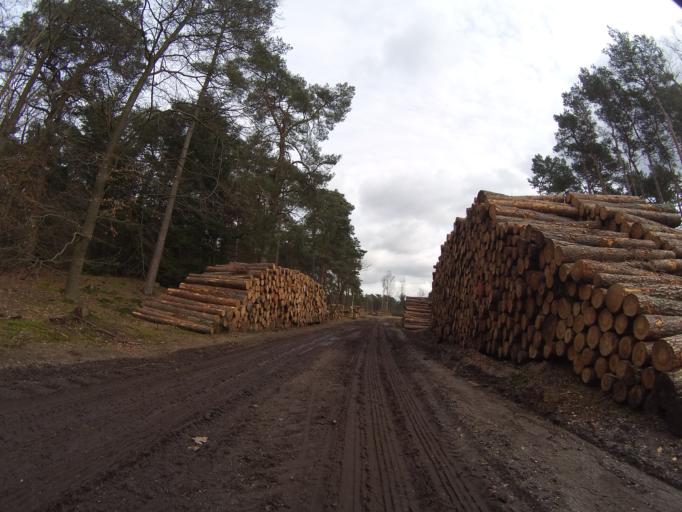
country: NL
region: Utrecht
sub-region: Gemeente Utrechtse Heuvelrug
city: Driebergen-Rijsenburg
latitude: 52.0697
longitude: 5.3037
